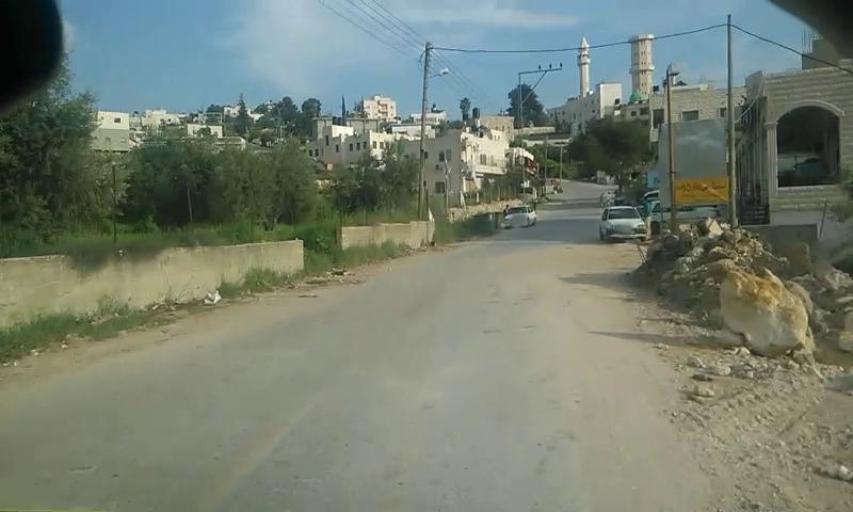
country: PS
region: West Bank
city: Nuba
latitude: 31.6092
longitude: 35.0361
